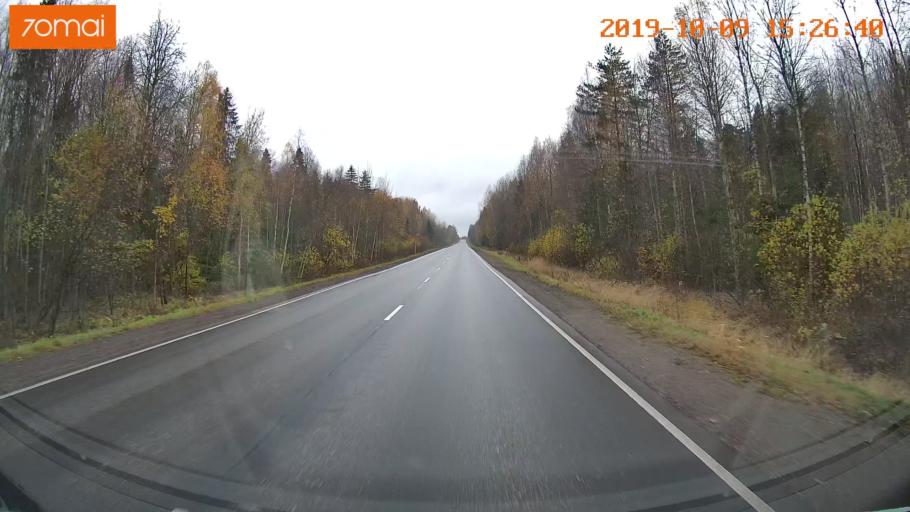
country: RU
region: Kostroma
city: Susanino
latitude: 58.0185
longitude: 41.3984
